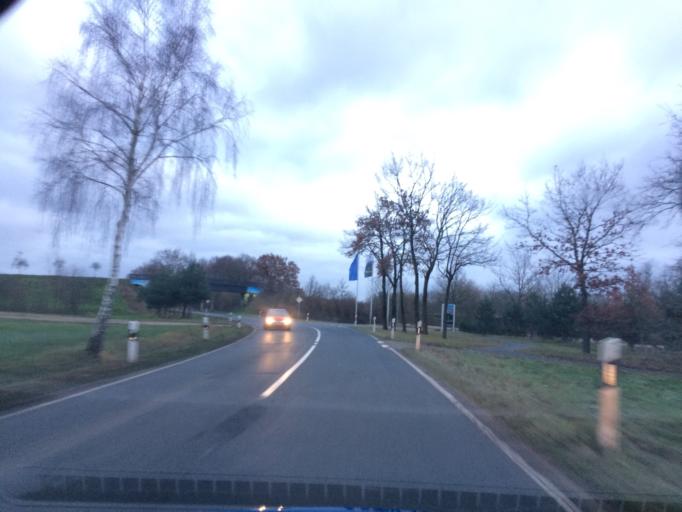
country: DE
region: Lower Saxony
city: Winsen
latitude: 53.3237
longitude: 10.2270
